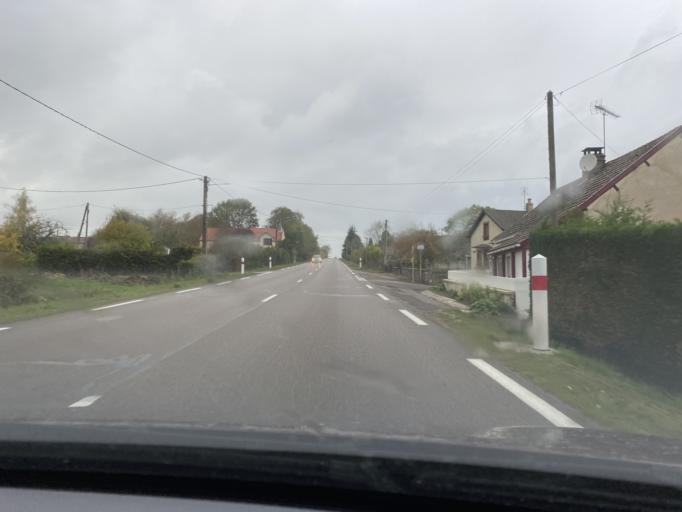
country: FR
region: Bourgogne
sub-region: Departement de la Cote-d'Or
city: Saulieu
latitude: 47.2916
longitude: 4.2201
